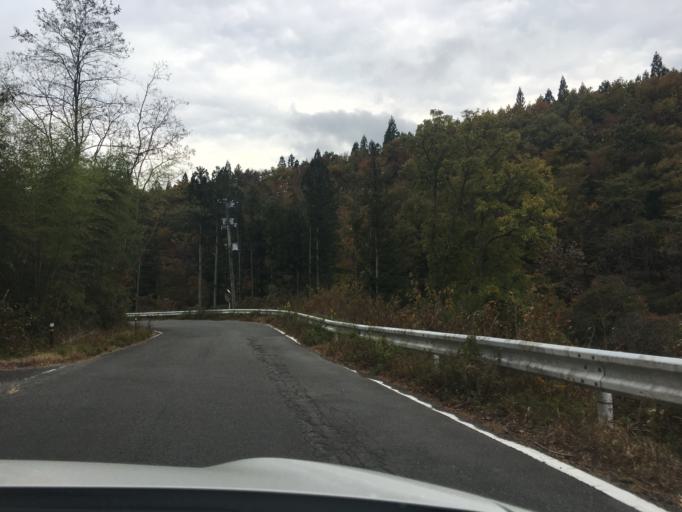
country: JP
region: Fukushima
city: Iwaki
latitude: 37.1290
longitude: 140.7758
